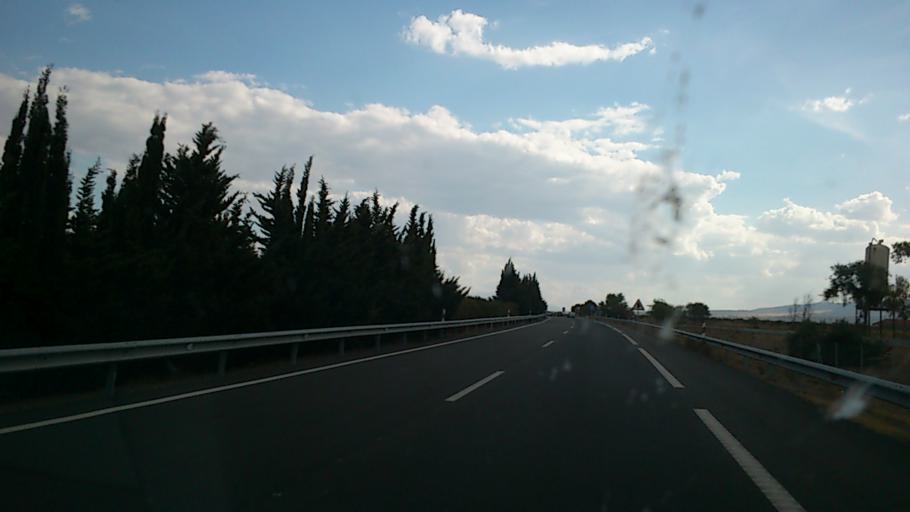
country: ES
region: La Rioja
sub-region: Provincia de La Rioja
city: Aldeanueva de Ebro
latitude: 42.2377
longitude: -1.9014
